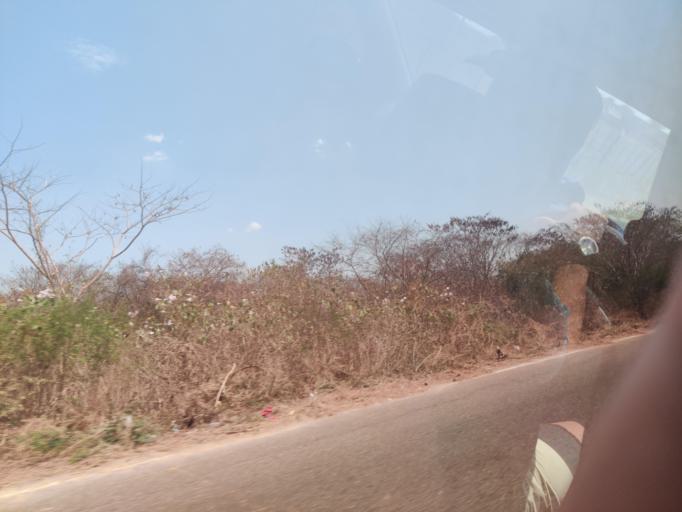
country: CO
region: Bolivar
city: Turbana
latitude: 10.2761
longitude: -75.5284
